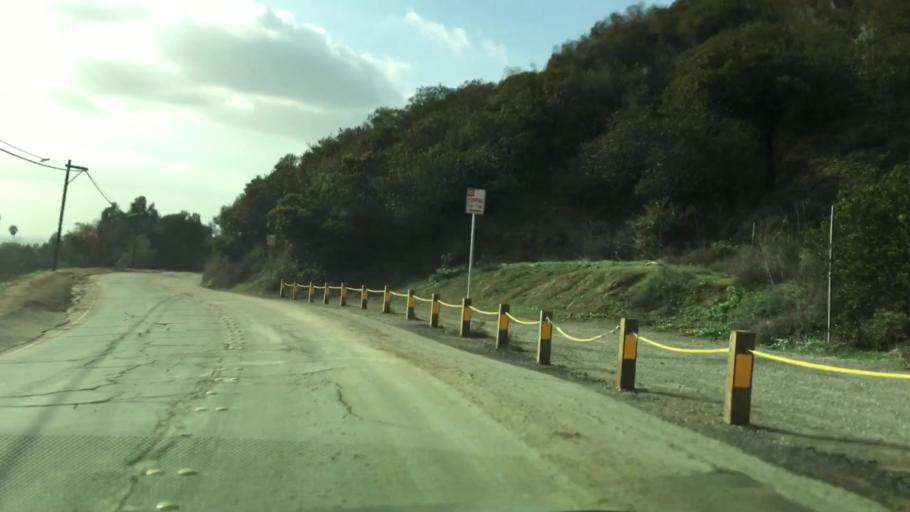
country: US
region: California
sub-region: Los Angeles County
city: Whittier
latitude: 33.9888
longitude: -118.0242
